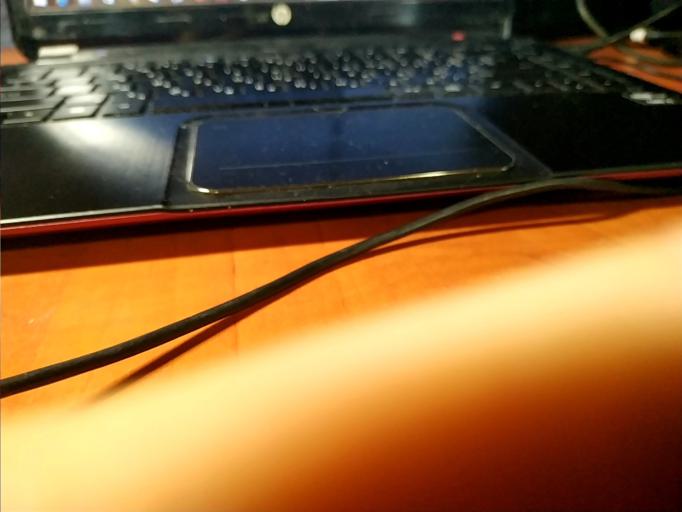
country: RU
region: Tverskaya
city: Rameshki
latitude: 57.1502
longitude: 36.0809
